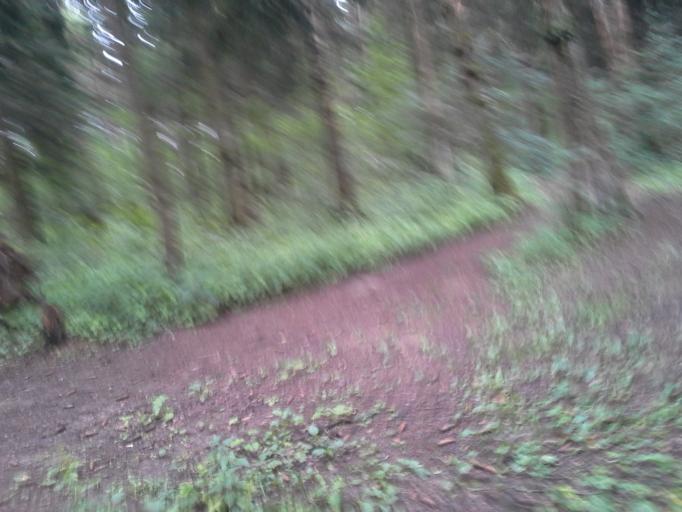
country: RU
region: Moscow
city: Novo-Peredelkino
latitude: 55.6423
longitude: 37.3045
